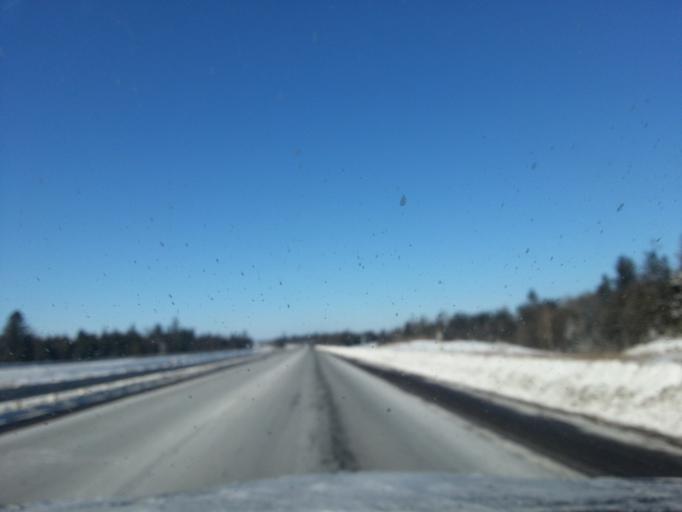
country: CA
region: Ontario
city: Arnprior
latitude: 45.3474
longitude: -76.2022
